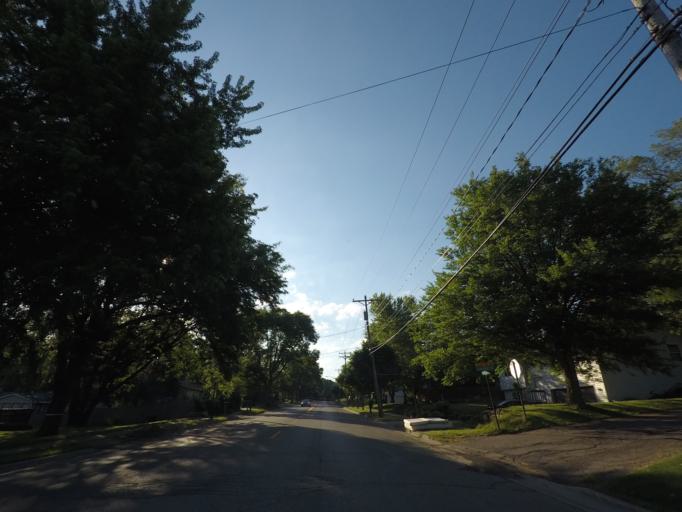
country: US
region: Wisconsin
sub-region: Dane County
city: Monona
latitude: 43.0351
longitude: -89.3721
